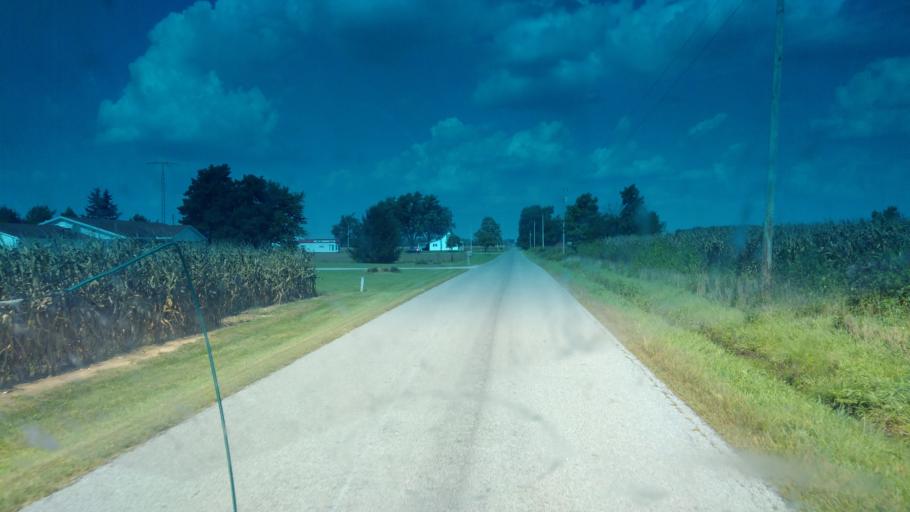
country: US
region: Ohio
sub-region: Hardin County
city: Ada
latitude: 40.6921
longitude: -83.8800
